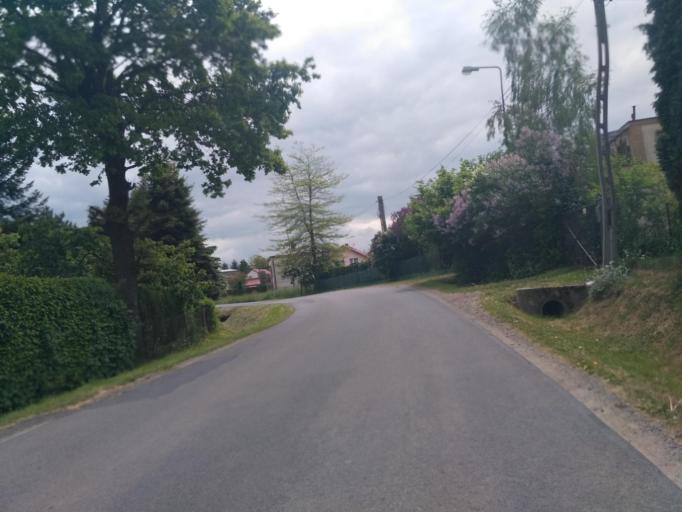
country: PL
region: Subcarpathian Voivodeship
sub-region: Powiat krosnienski
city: Jedlicze
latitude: 49.7069
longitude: 21.6363
